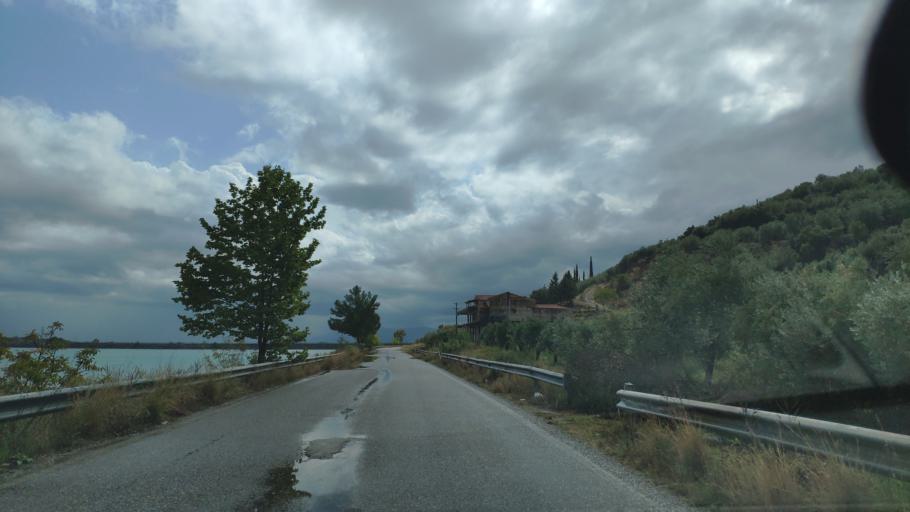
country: GR
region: West Greece
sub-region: Nomos Aitolias kai Akarnanias
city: Neapolis
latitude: 38.6832
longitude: 21.3230
